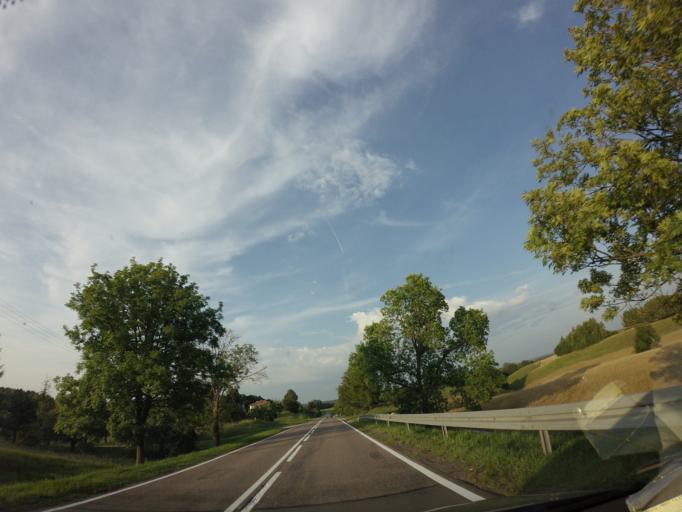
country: PL
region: Podlasie
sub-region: Powiat sejnenski
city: Sejny
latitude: 54.1240
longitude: 23.4363
